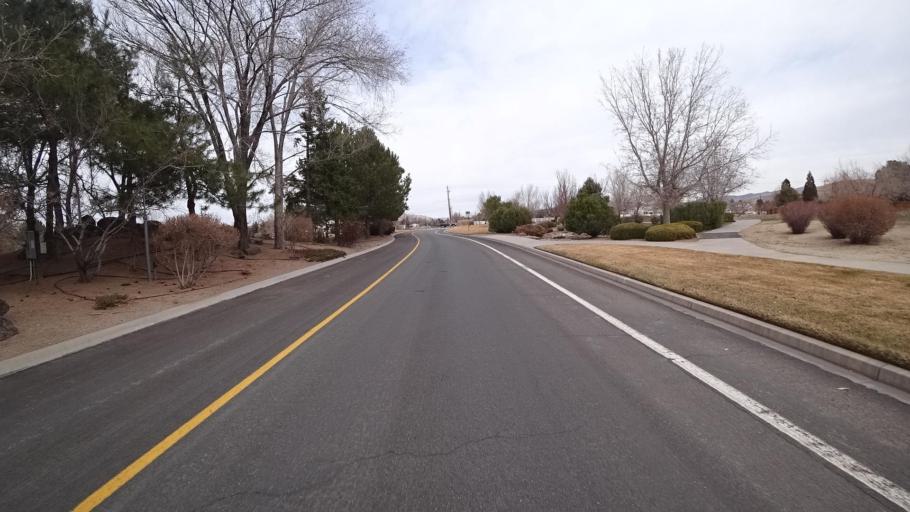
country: US
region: Nevada
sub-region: Washoe County
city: Spanish Springs
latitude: 39.6349
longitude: -119.6911
